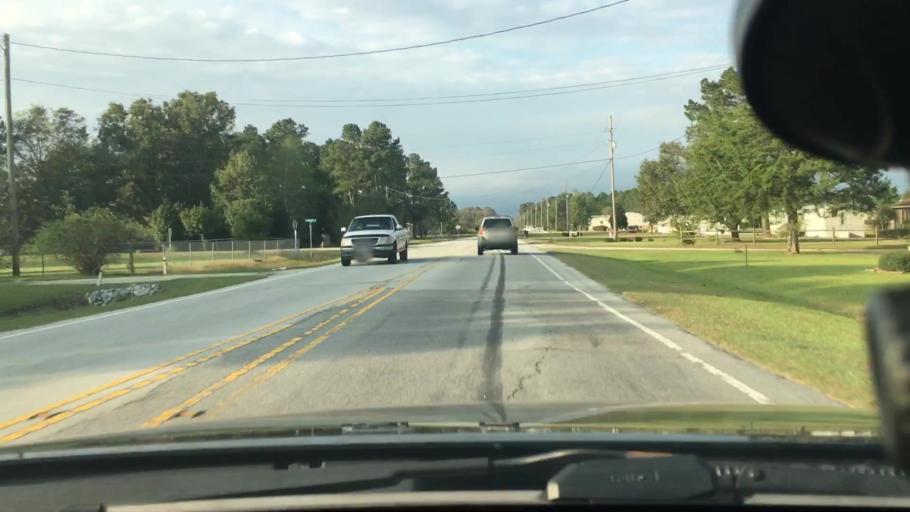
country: US
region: North Carolina
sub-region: Pitt County
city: Windsor
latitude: 35.5154
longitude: -77.3191
